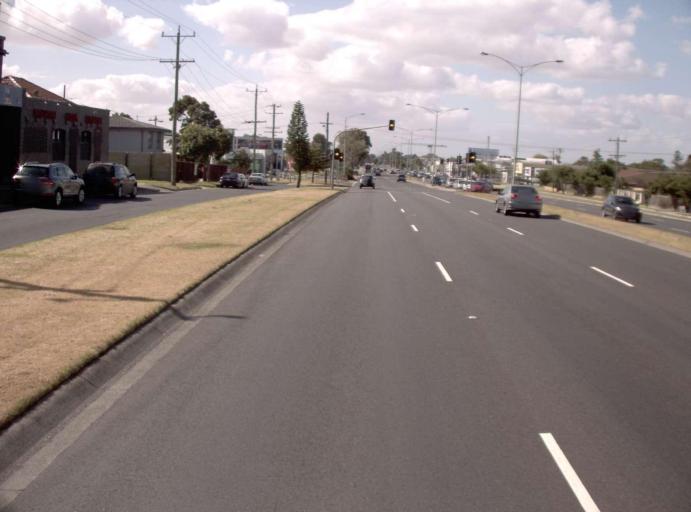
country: AU
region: Victoria
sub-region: Kingston
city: Mentone
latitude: -37.9728
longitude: 145.0636
